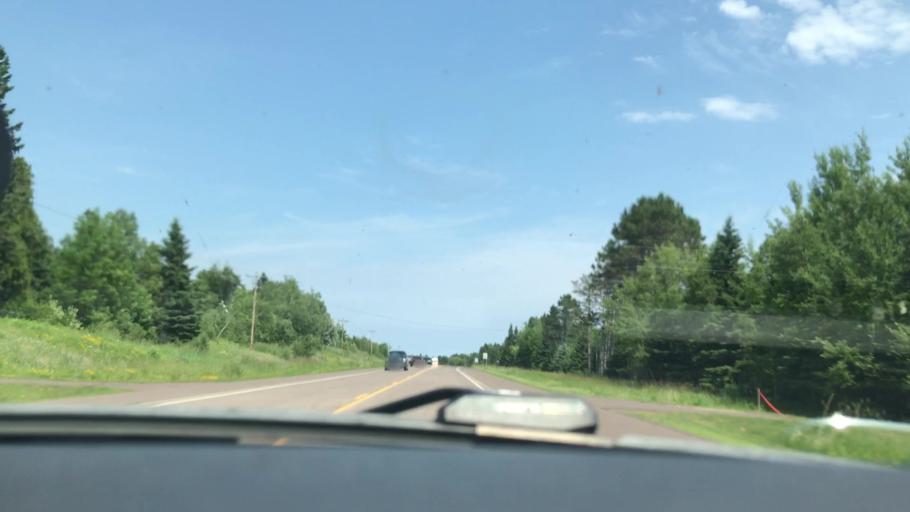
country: US
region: Minnesota
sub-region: Lake County
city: Two Harbors
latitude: 47.1222
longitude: -91.5008
